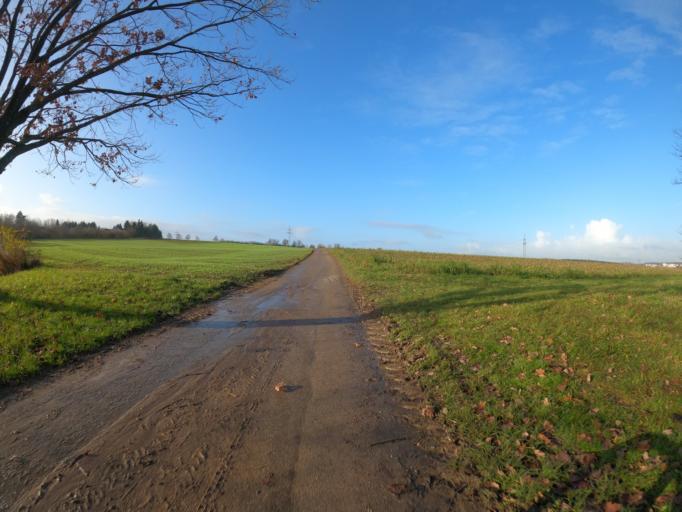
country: DE
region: Baden-Wuerttemberg
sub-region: Regierungsbezirk Stuttgart
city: Hattenhofen
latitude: 48.6709
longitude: 9.5622
